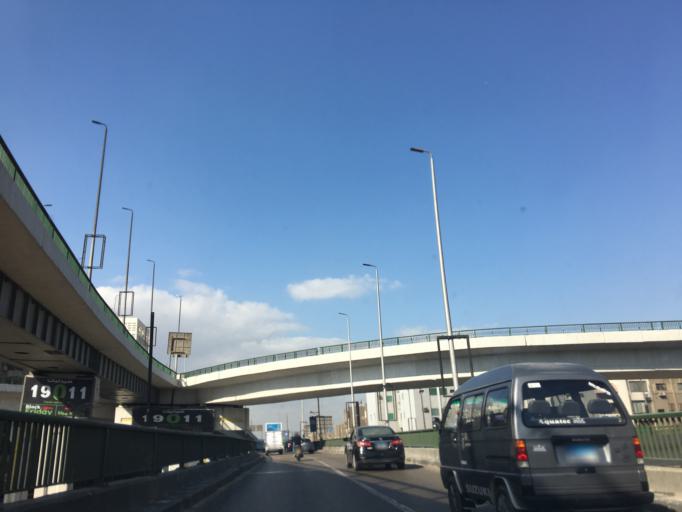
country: EG
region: Muhafazat al Qahirah
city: Cairo
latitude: 30.0582
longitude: 31.3033
